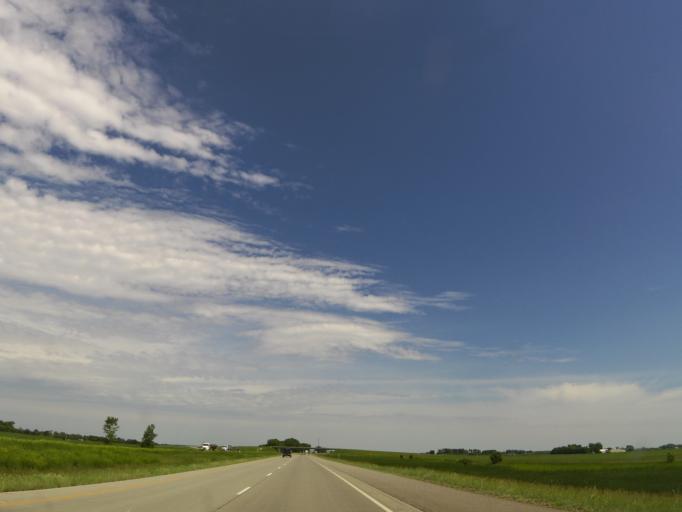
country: US
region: North Dakota
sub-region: Grand Forks County
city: Grand Forks
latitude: 47.7245
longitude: -97.0769
